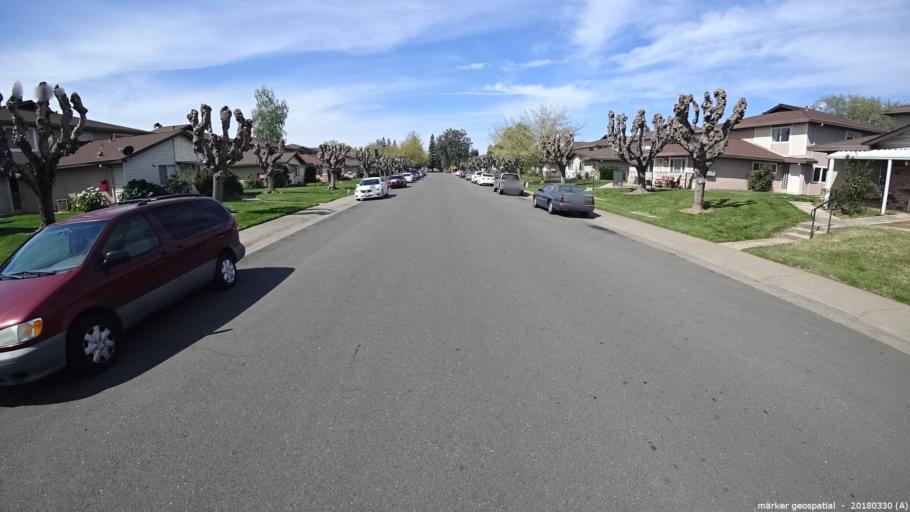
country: US
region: California
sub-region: Sacramento County
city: Rosemont
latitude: 38.5591
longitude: -121.3691
